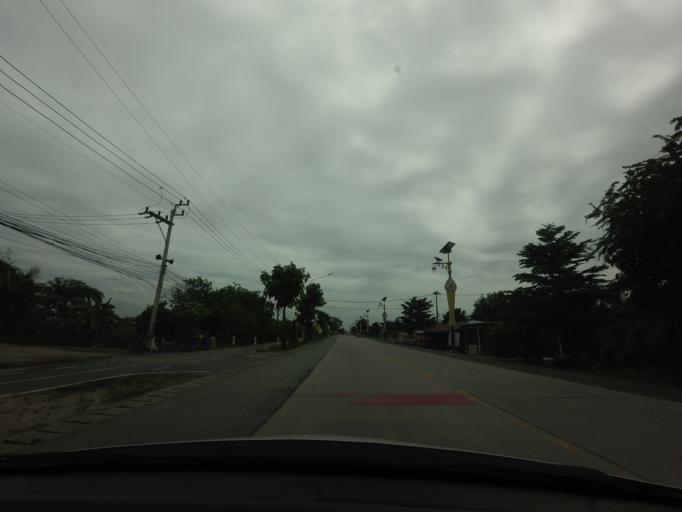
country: TH
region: Pathum Thani
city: Lam Luk Ka
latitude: 13.9310
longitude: 100.7464
